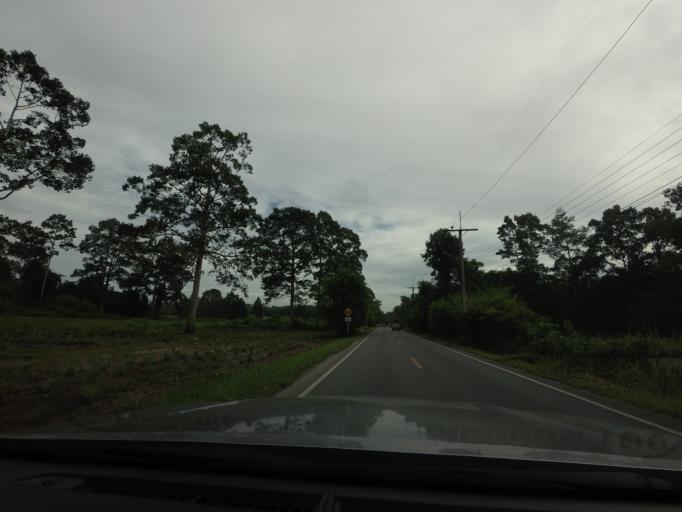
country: TH
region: Nakhon Si Thammarat
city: Phra Phrom
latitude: 8.2765
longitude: 99.9441
